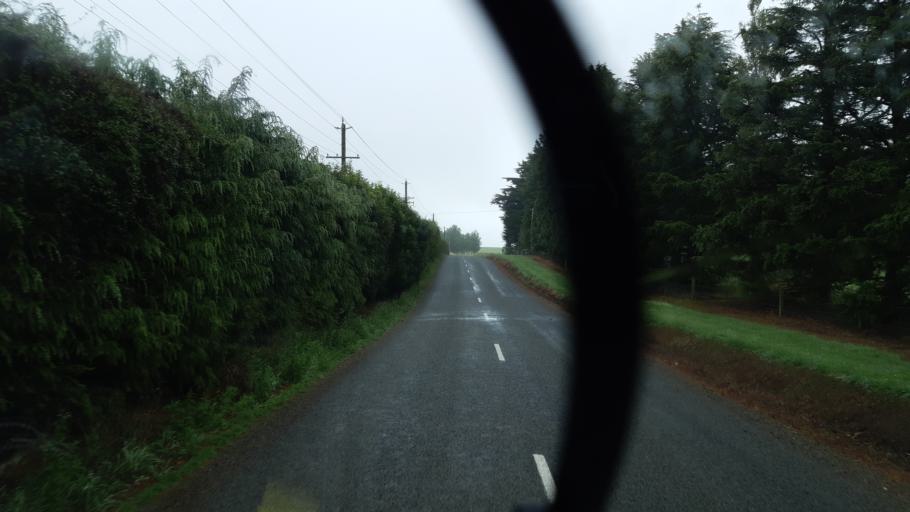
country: NZ
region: Otago
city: Oamaru
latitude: -44.9368
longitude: 170.7185
